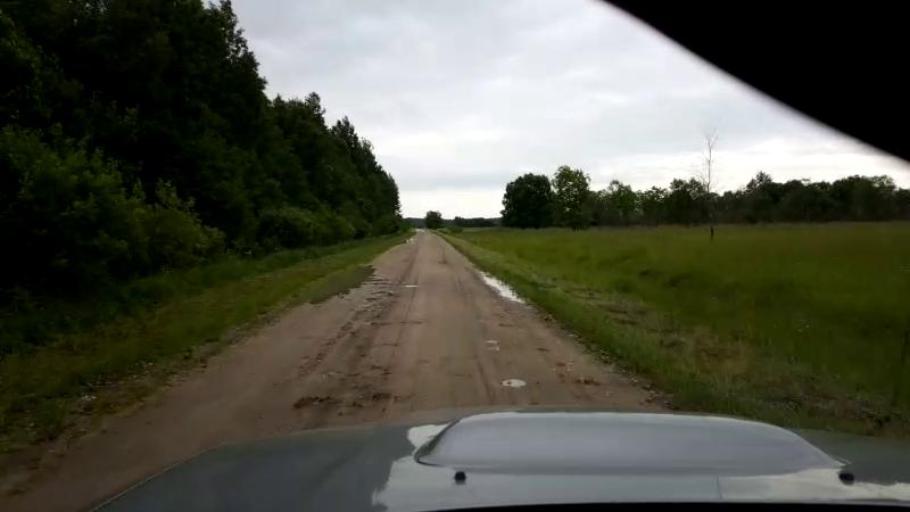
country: EE
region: Paernumaa
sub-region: Halinga vald
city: Parnu-Jaagupi
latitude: 58.5446
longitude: 24.5770
